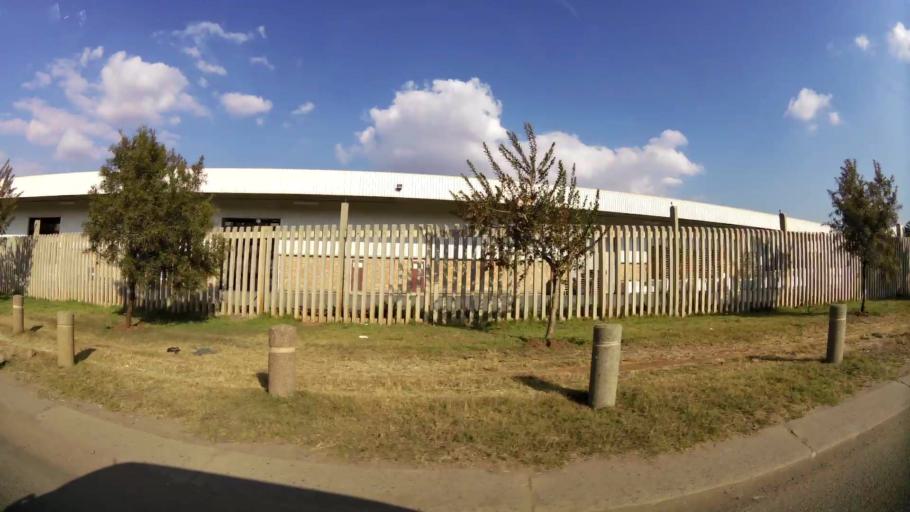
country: ZA
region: Gauteng
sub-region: Ekurhuleni Metropolitan Municipality
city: Tembisa
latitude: -25.9417
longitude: 28.2316
